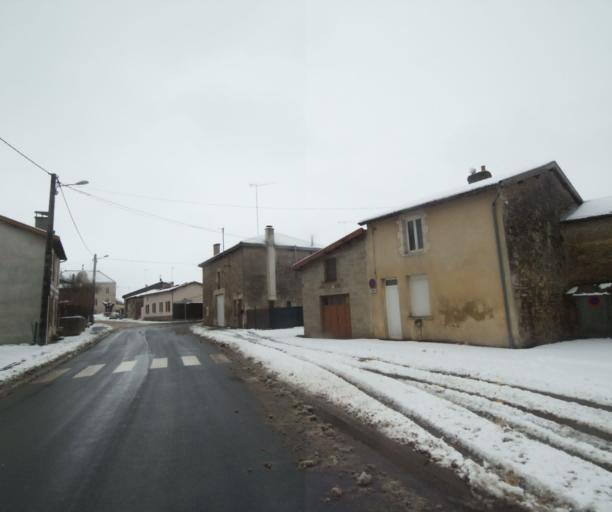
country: FR
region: Champagne-Ardenne
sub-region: Departement de la Haute-Marne
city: Wassy
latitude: 48.4398
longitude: 4.9581
